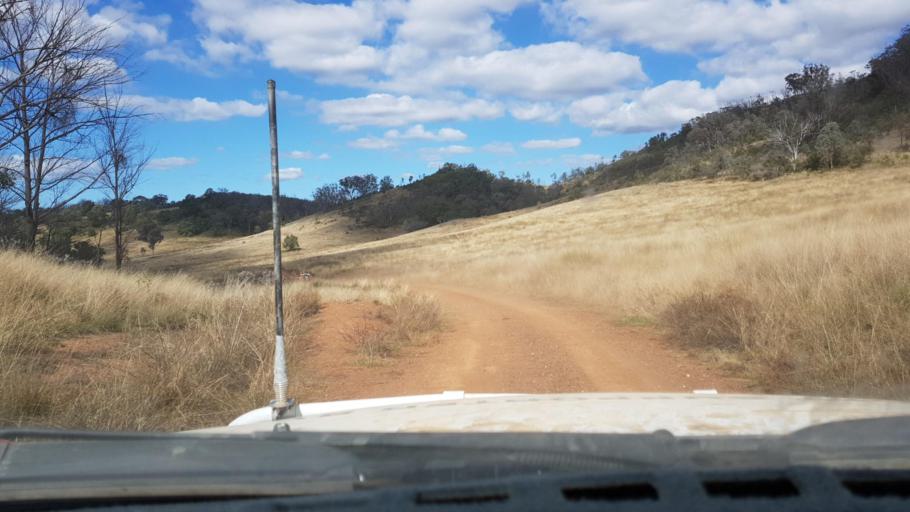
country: AU
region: New South Wales
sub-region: Tamworth Municipality
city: Manilla
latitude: -30.4372
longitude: 150.8276
